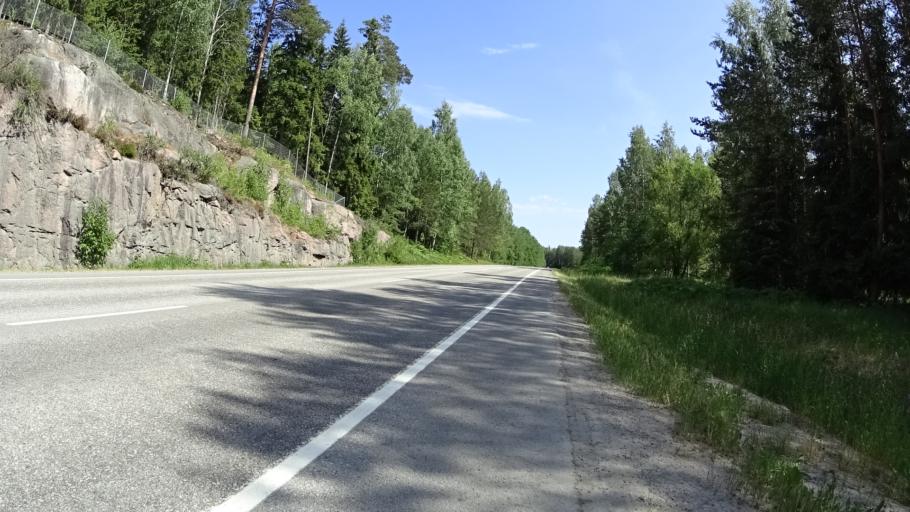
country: FI
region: Uusimaa
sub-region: Raaseporin
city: Karis
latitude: 60.0911
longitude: 23.6413
